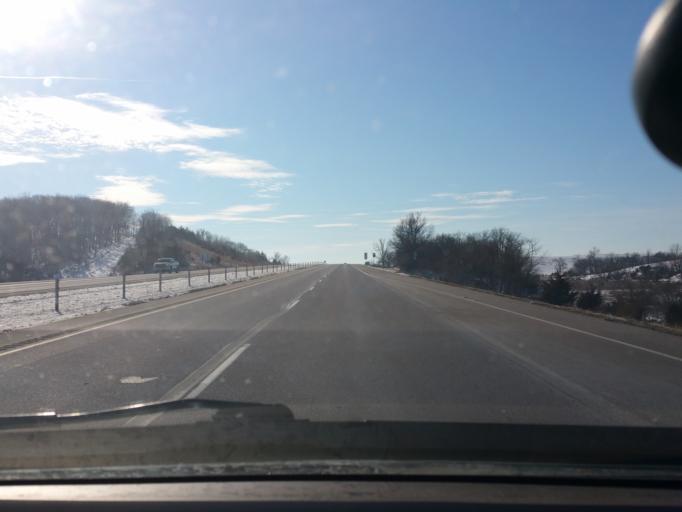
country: US
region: Iowa
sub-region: Clarke County
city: Osceola
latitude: 41.0662
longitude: -93.7815
